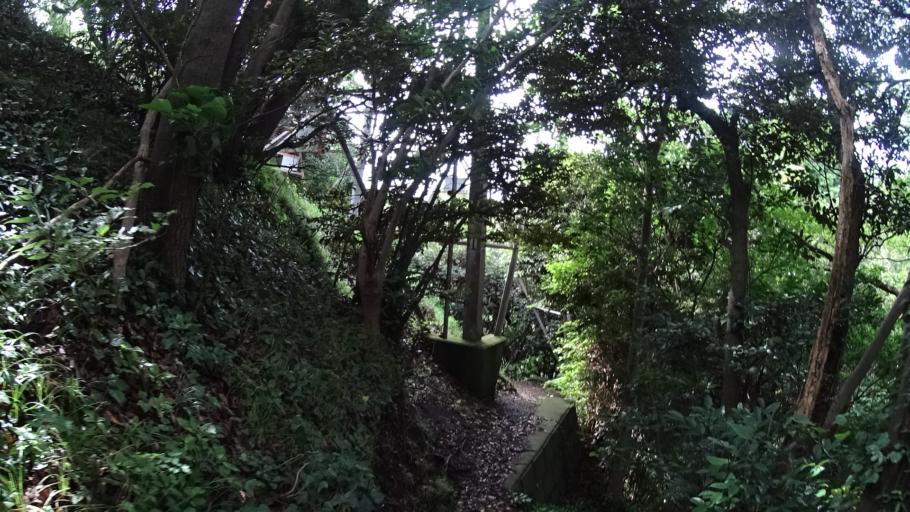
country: JP
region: Kanagawa
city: Yokosuka
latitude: 35.2713
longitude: 139.6333
